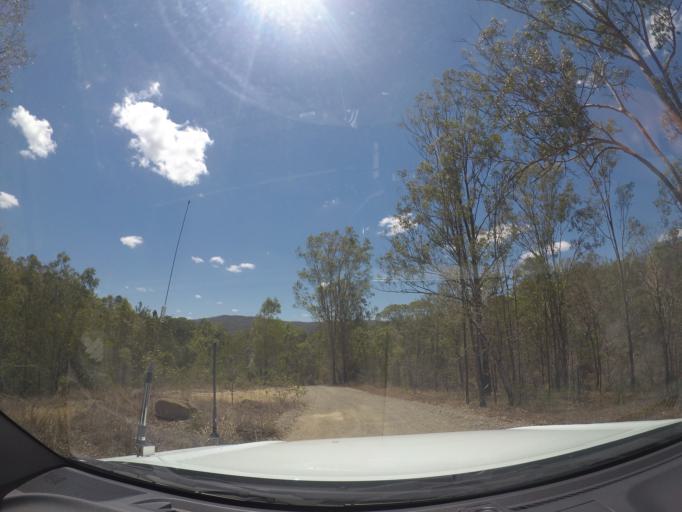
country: AU
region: Queensland
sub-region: Ipswich
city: Springfield Lakes
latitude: -27.8201
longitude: 152.8454
